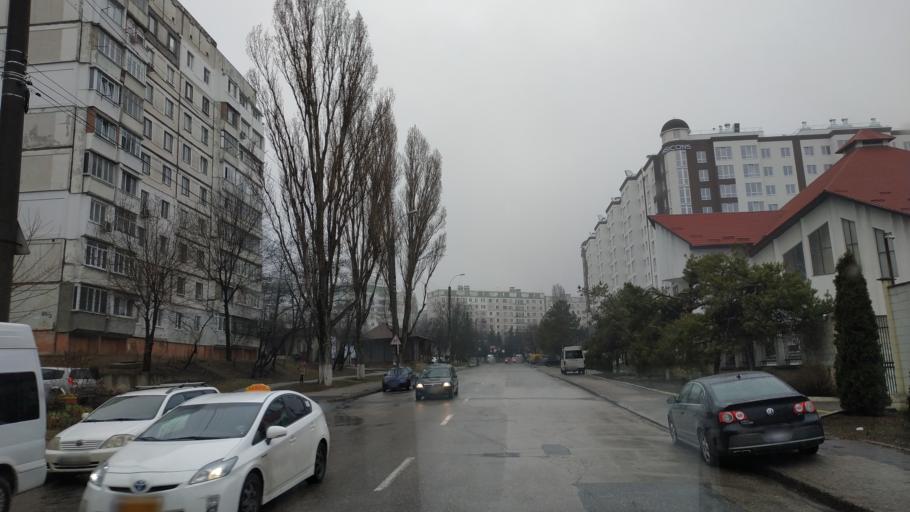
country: MD
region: Chisinau
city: Vatra
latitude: 47.0421
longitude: 28.7727
